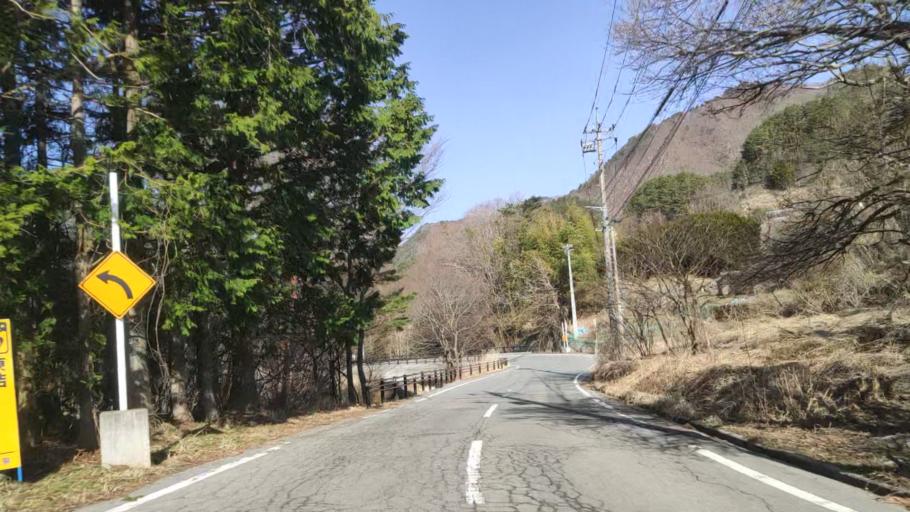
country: JP
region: Yamanashi
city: Fujikawaguchiko
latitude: 35.5527
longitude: 138.6873
